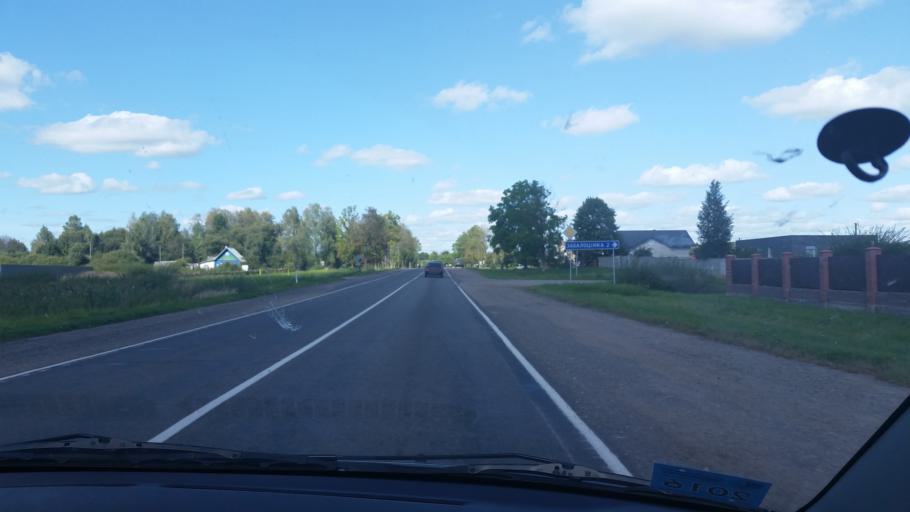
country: BY
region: Vitebsk
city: Vitebsk
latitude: 55.1127
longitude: 30.2826
